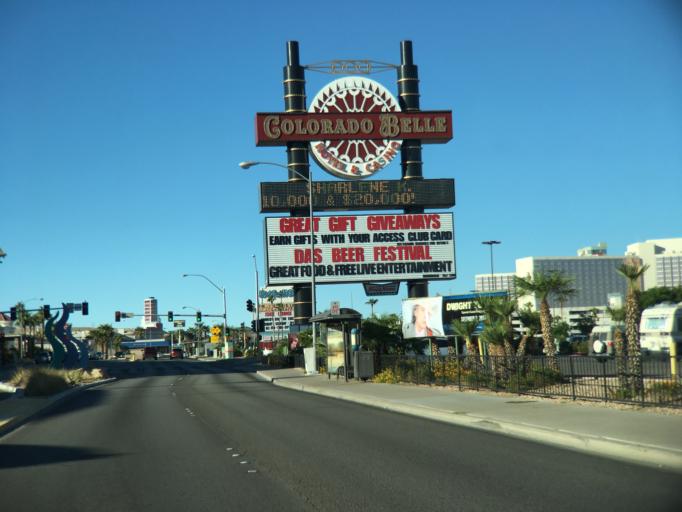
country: US
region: Nevada
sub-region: Clark County
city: Laughlin
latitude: 35.1572
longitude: -114.5747
